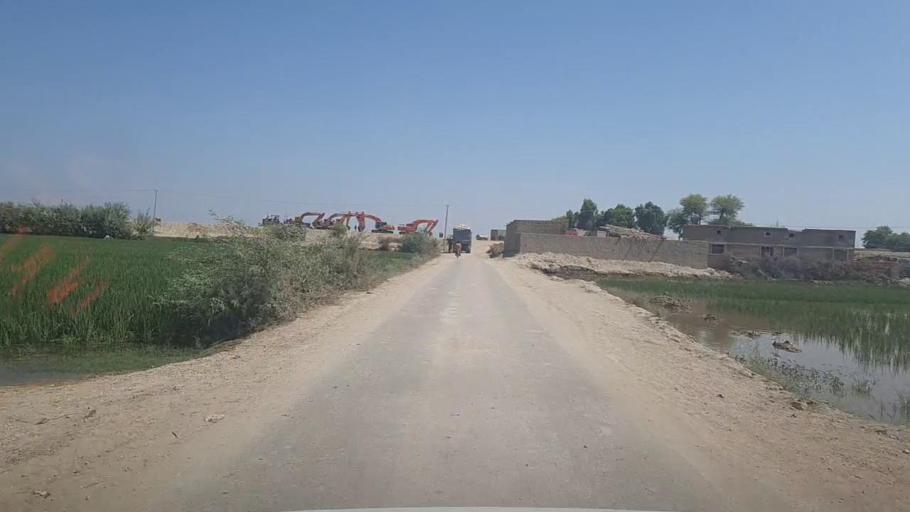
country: PK
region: Sindh
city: Kashmor
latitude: 28.2805
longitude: 69.4432
